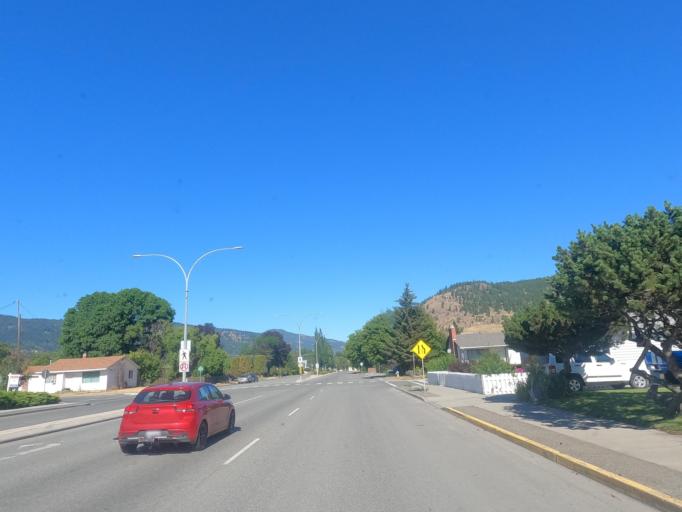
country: CA
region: British Columbia
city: Merritt
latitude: 50.1124
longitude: -120.7903
